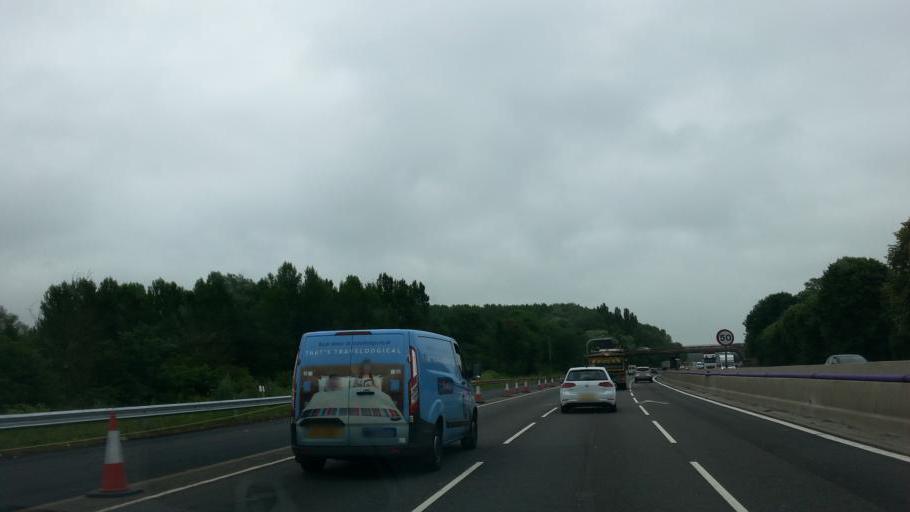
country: GB
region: England
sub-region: Northamptonshire
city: Long Buckby
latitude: 52.2768
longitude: -1.0942
